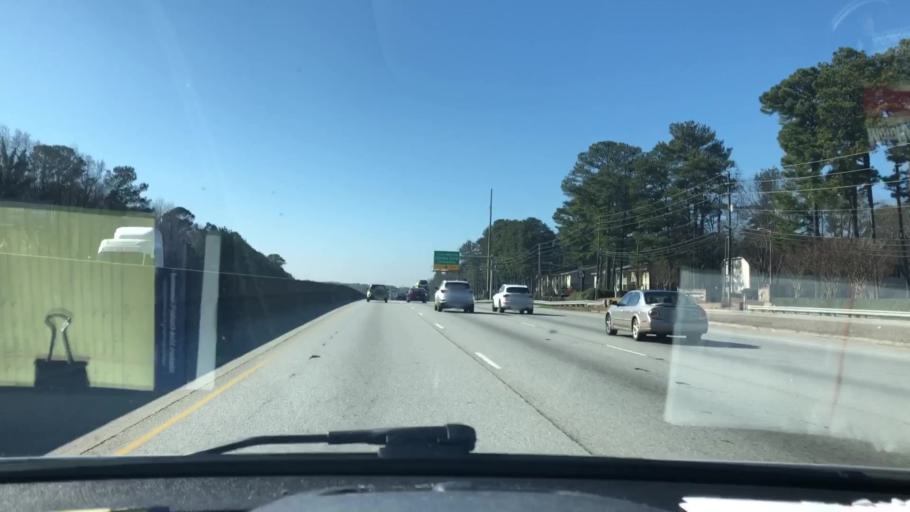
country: US
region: Georgia
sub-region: DeKalb County
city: Doraville
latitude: 33.9282
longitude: -84.2718
